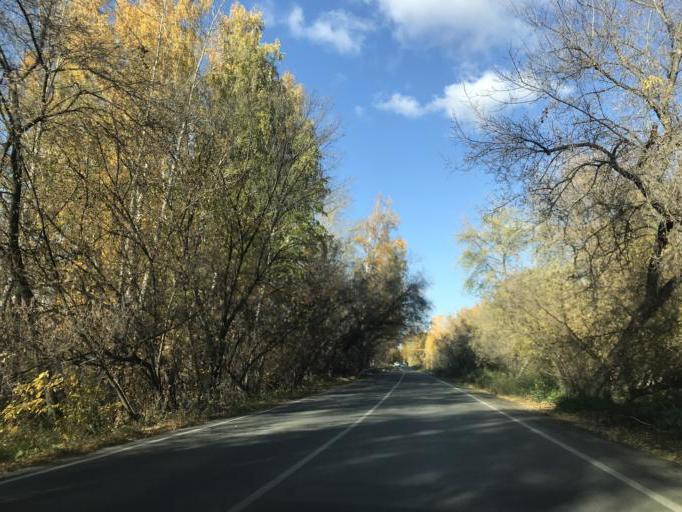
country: RU
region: Chelyabinsk
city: Dolgoderevenskoye
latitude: 55.2625
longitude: 61.3643
